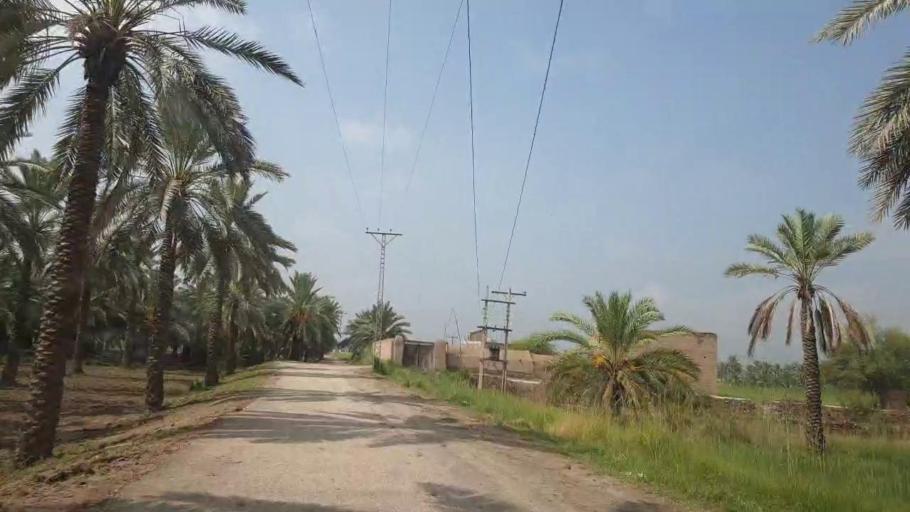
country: PK
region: Sindh
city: Khairpur
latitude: 27.5576
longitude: 68.7591
